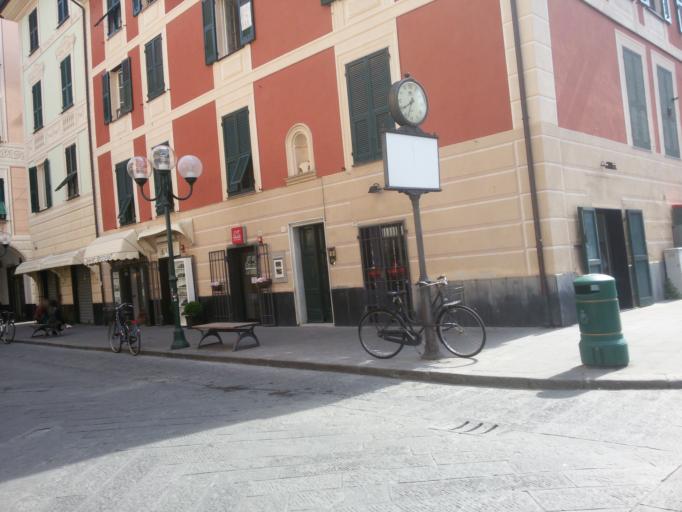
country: IT
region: Liguria
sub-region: Provincia di Genova
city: Chiavari
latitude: 44.3188
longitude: 9.3217
